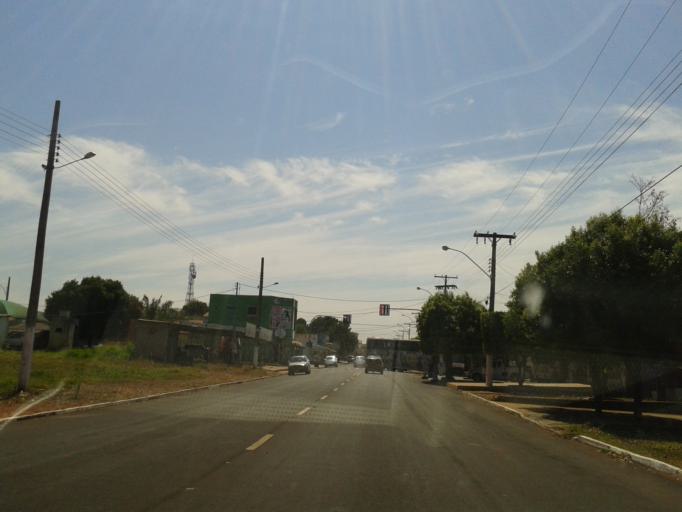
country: BR
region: Minas Gerais
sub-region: Santa Vitoria
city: Santa Vitoria
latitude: -18.9997
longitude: -50.5510
